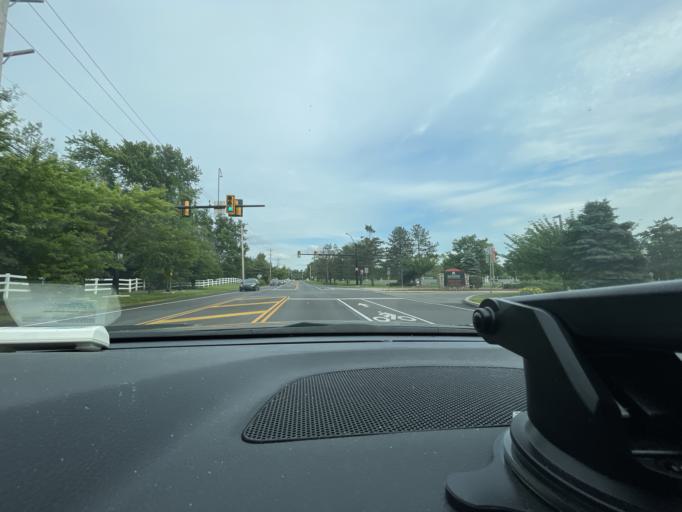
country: US
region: Pennsylvania
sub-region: Montgomery County
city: Blue Bell
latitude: 40.1766
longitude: -75.2729
